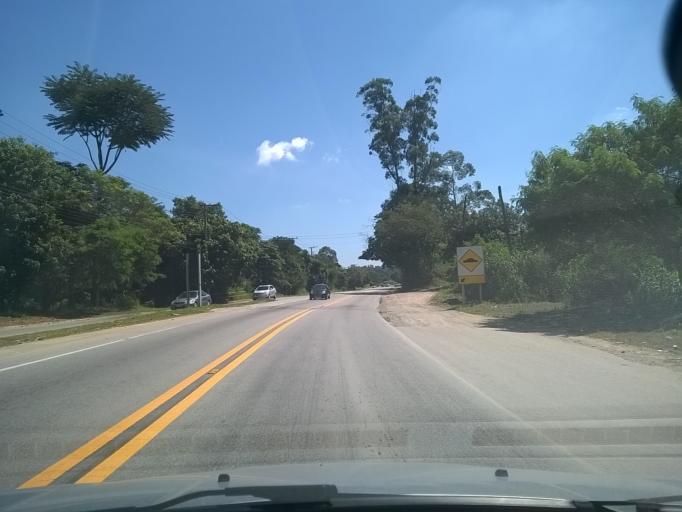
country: BR
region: Sao Paulo
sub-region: Varzea Paulista
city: Varzea Paulista
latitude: -23.2415
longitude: -46.8548
